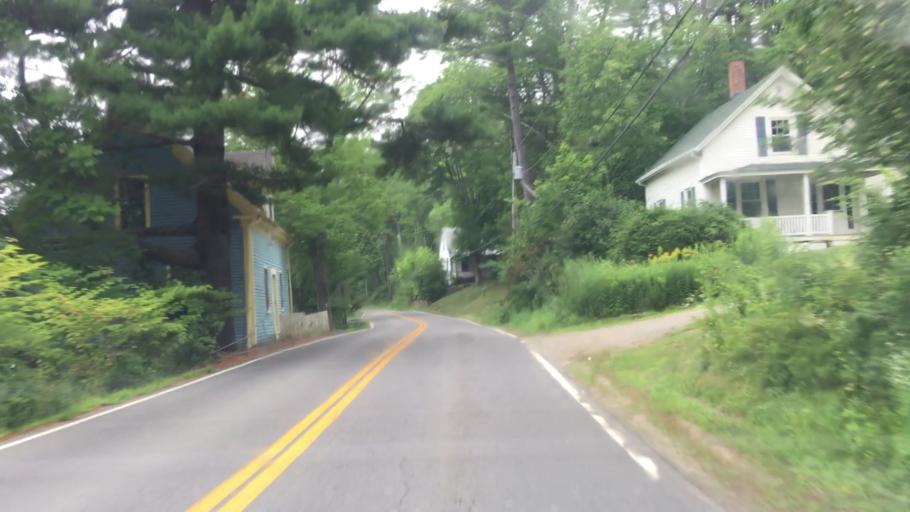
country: US
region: Maine
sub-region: Lincoln County
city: Wiscasset
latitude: 43.9906
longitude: -69.6495
